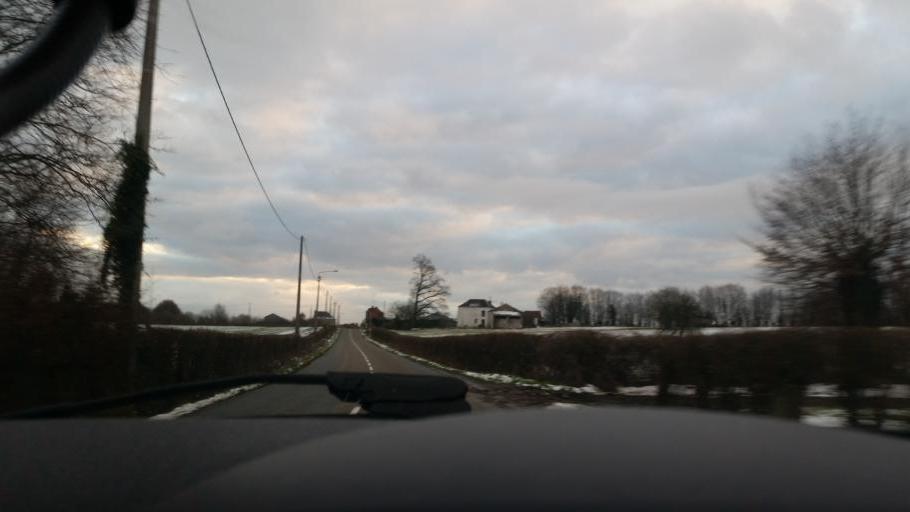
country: FR
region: Nord-Pas-de-Calais
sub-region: Departement du Nord
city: Marpent
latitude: 50.2445
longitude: 4.0966
